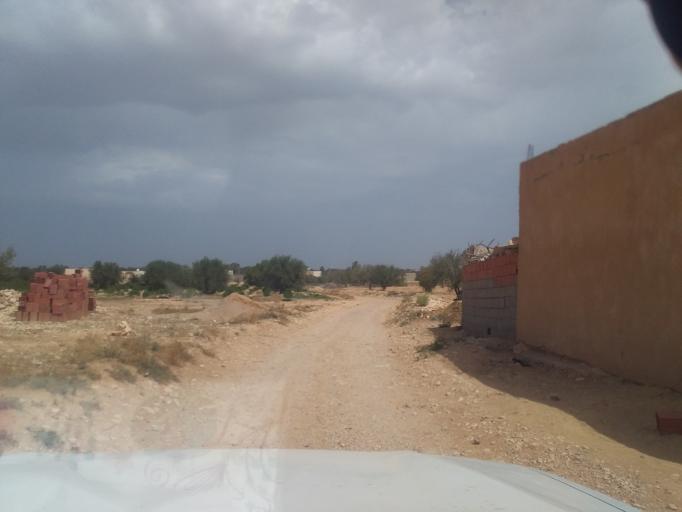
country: TN
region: Madanin
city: Medenine
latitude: 33.5887
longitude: 10.3240
